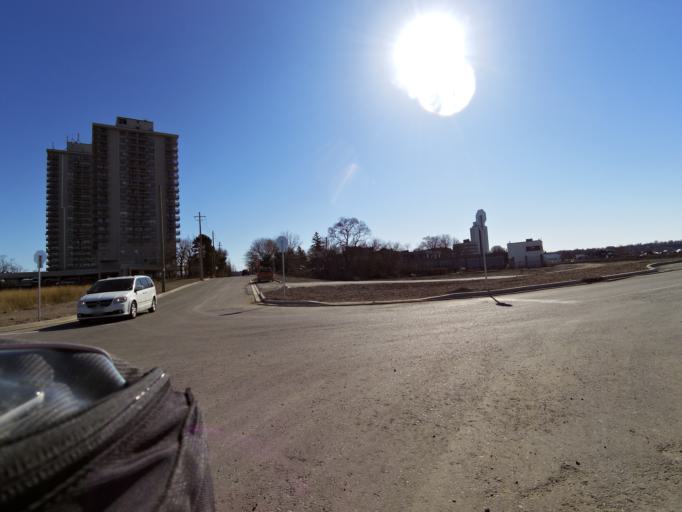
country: CA
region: Ontario
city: Hamilton
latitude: 43.2756
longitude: -79.8579
